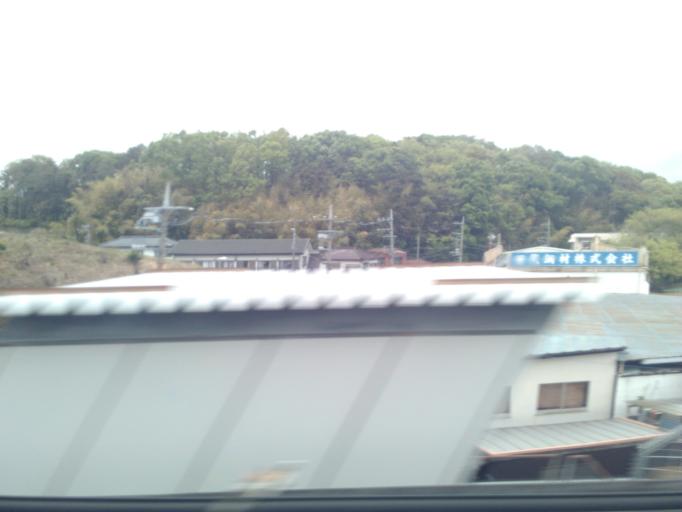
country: JP
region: Kanagawa
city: Yokohama
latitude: 35.4839
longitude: 139.5803
